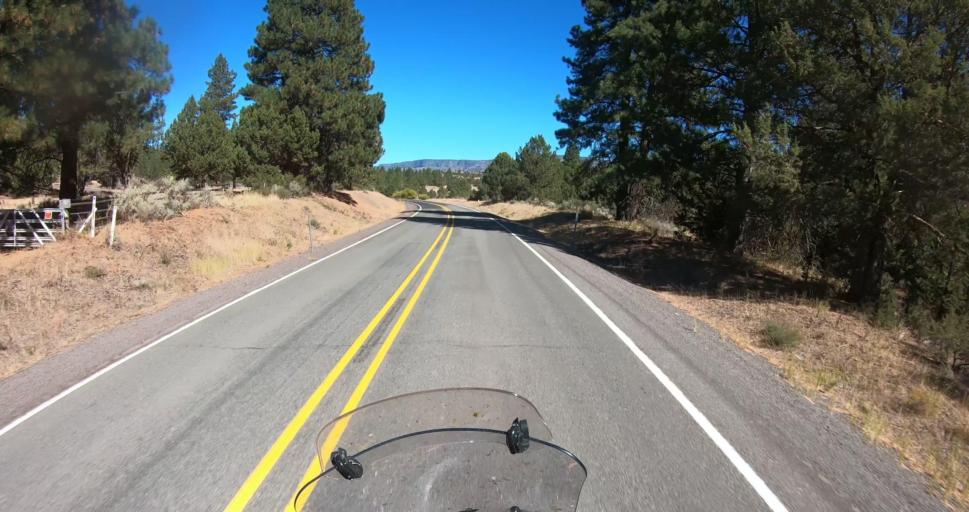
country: US
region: Oregon
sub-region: Lake County
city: Lakeview
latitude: 42.3971
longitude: -120.2943
